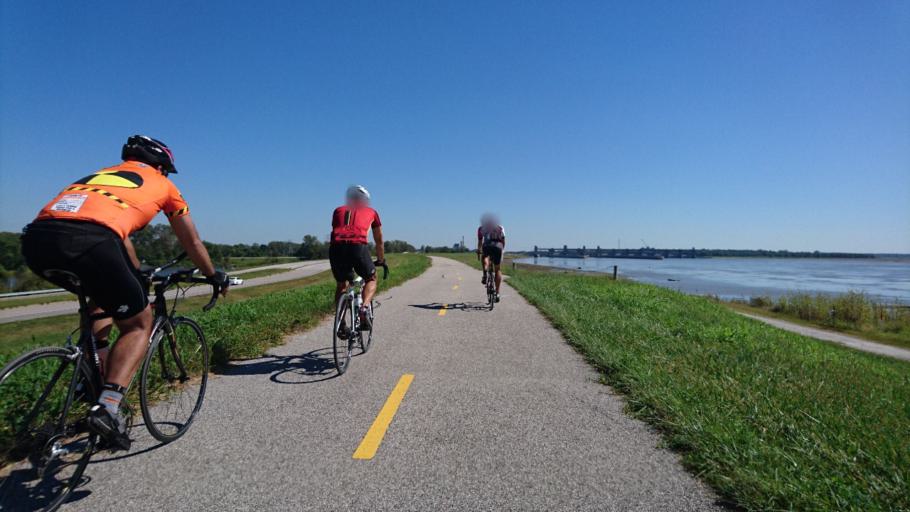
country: US
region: Illinois
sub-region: Madison County
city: Alton
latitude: 38.8809
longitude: -90.1663
